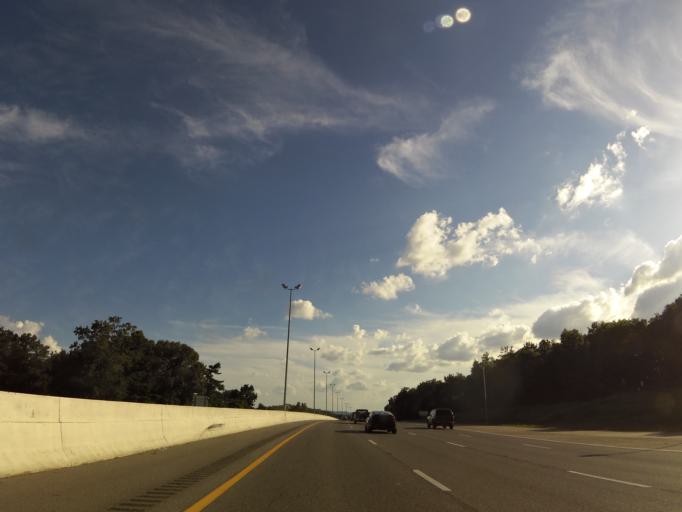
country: US
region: Tennessee
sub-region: Davidson County
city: Lakewood
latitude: 36.1875
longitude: -86.6894
